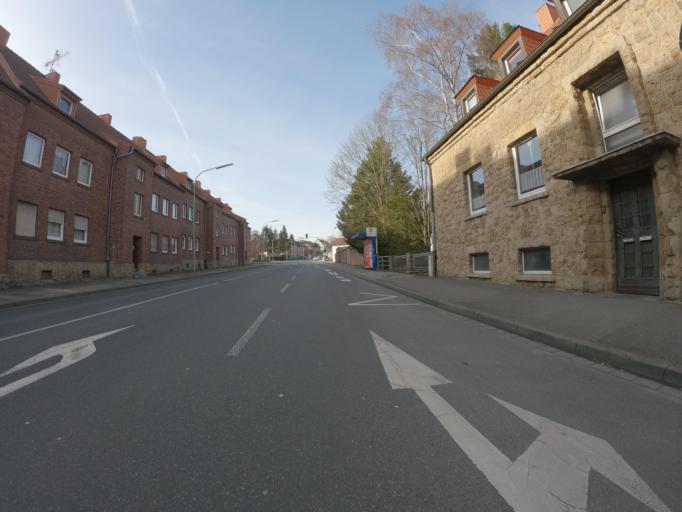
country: DE
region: North Rhine-Westphalia
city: Stolberg
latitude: 50.7573
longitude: 6.2196
